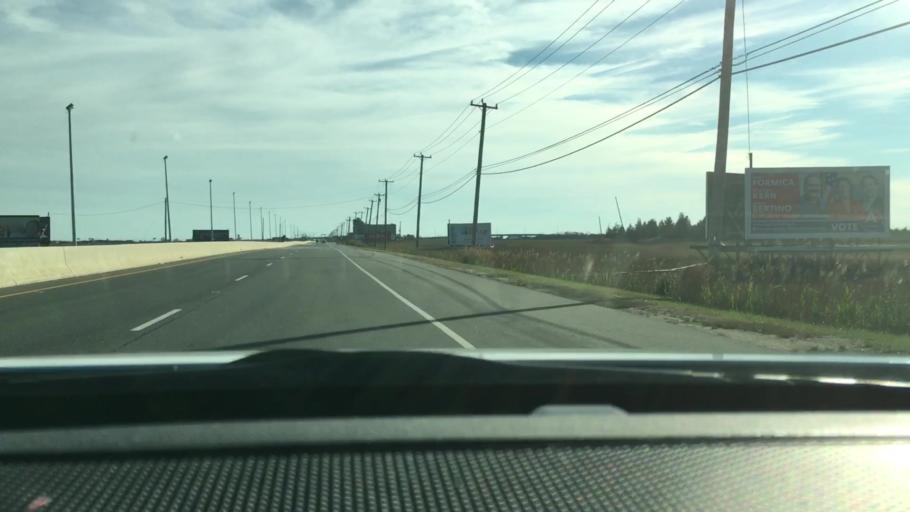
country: US
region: New Jersey
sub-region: Atlantic County
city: Absecon
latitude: 39.4137
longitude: -74.4915
